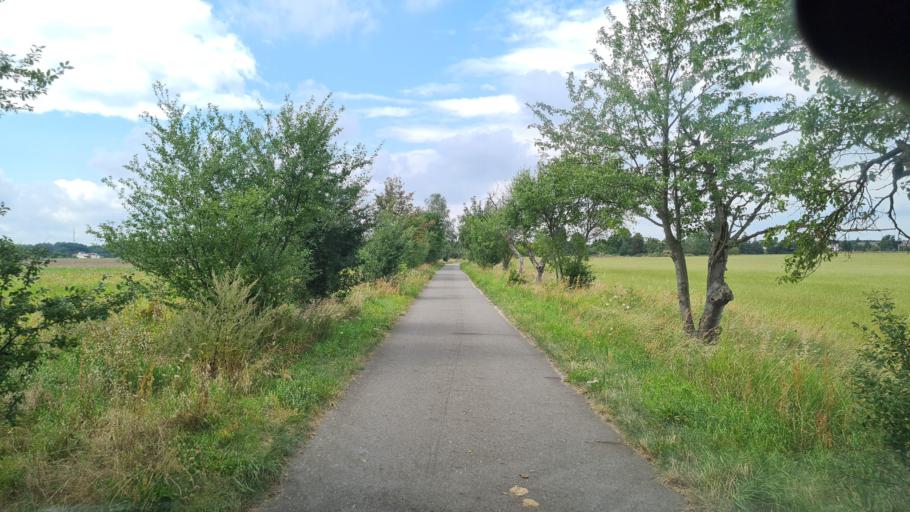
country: DE
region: Brandenburg
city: Sallgast
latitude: 51.5880
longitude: 13.8610
